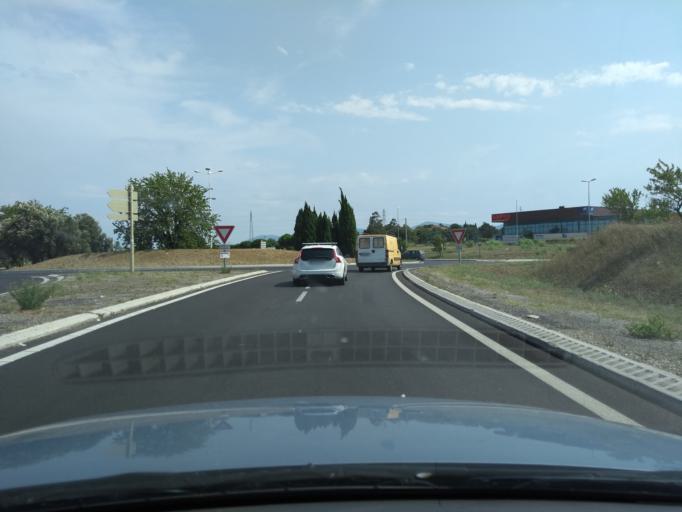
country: FR
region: Languedoc-Roussillon
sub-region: Departement des Pyrenees-Orientales
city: Perpignan
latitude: 42.6692
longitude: 2.8969
